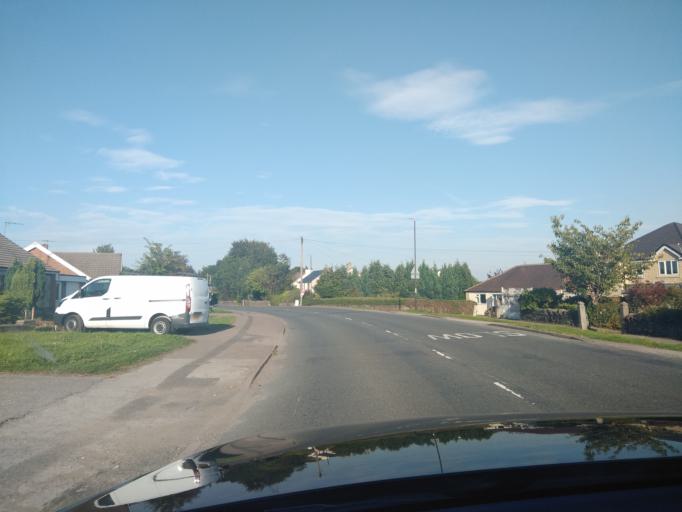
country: GB
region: England
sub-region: Derbyshire
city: Dronfield
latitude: 53.3058
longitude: -1.4886
